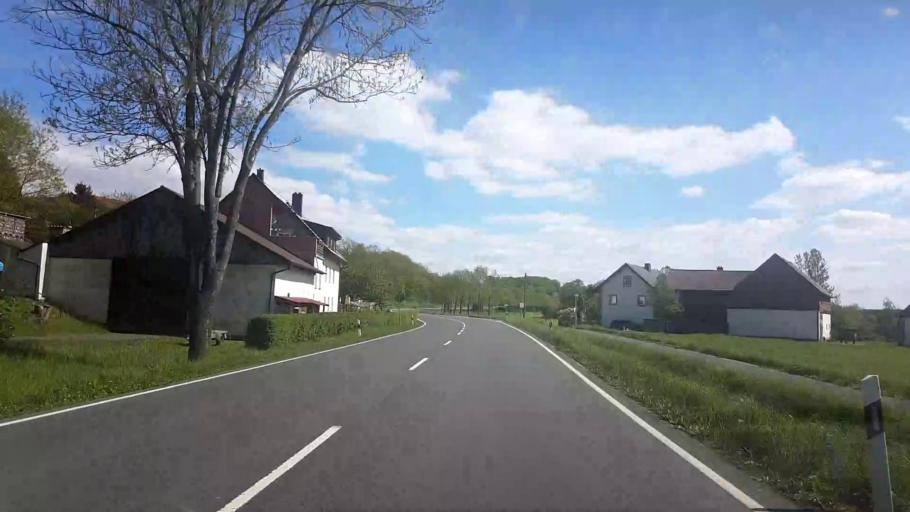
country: DE
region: Bavaria
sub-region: Upper Franconia
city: Rattelsdorf
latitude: 50.0630
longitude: 10.8740
